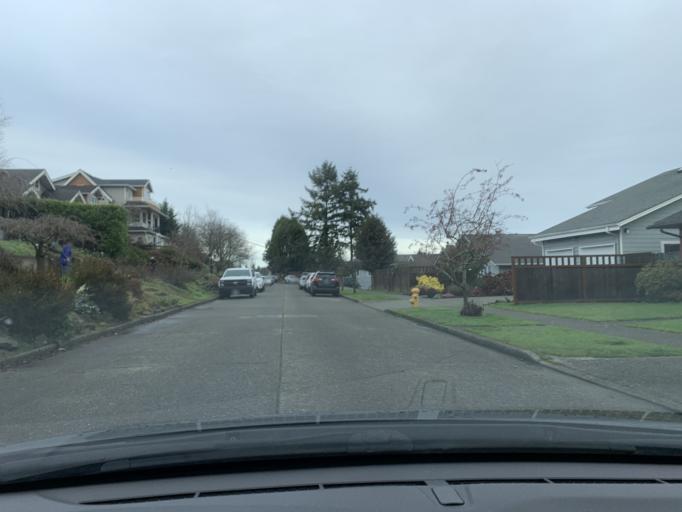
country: US
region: Washington
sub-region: King County
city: White Center
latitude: 47.5566
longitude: -122.3841
